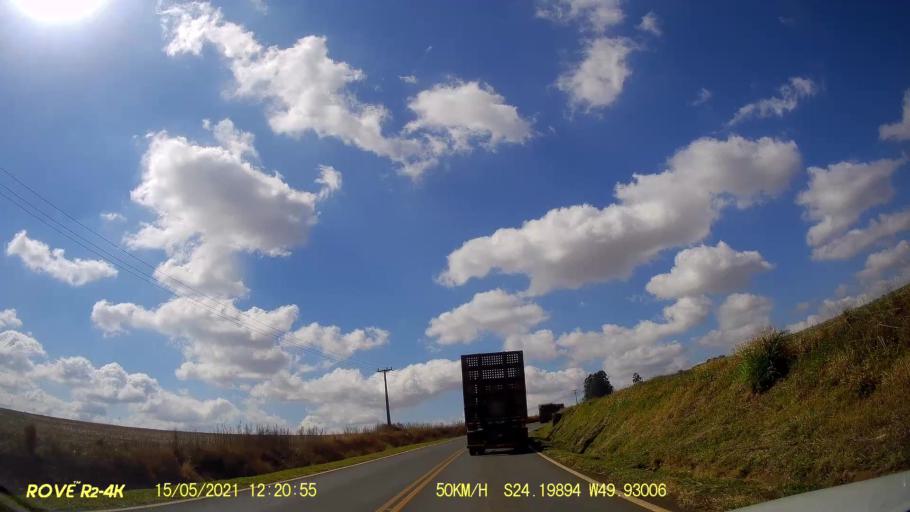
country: BR
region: Parana
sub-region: Jaguariaiva
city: Jaguariaiva
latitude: -24.1992
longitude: -49.9303
